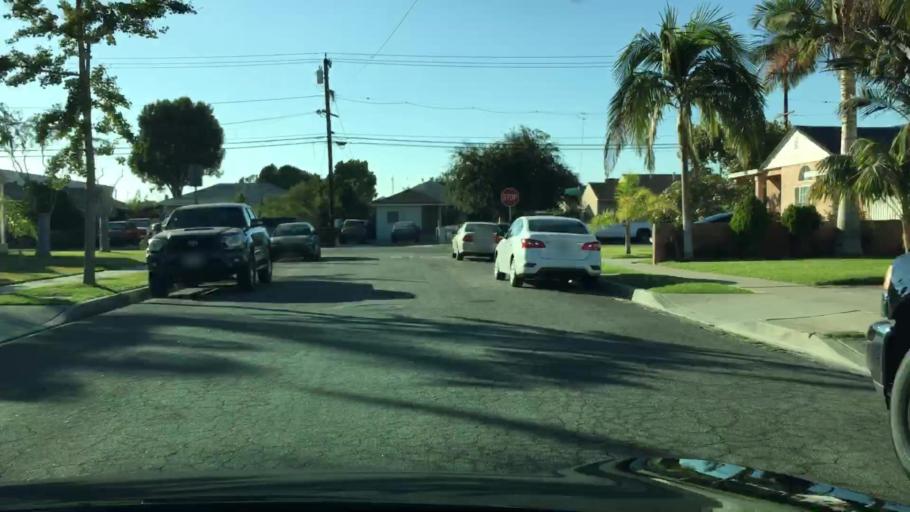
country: US
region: California
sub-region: Los Angeles County
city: Pico Rivera
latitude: 33.9827
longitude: -118.0845
